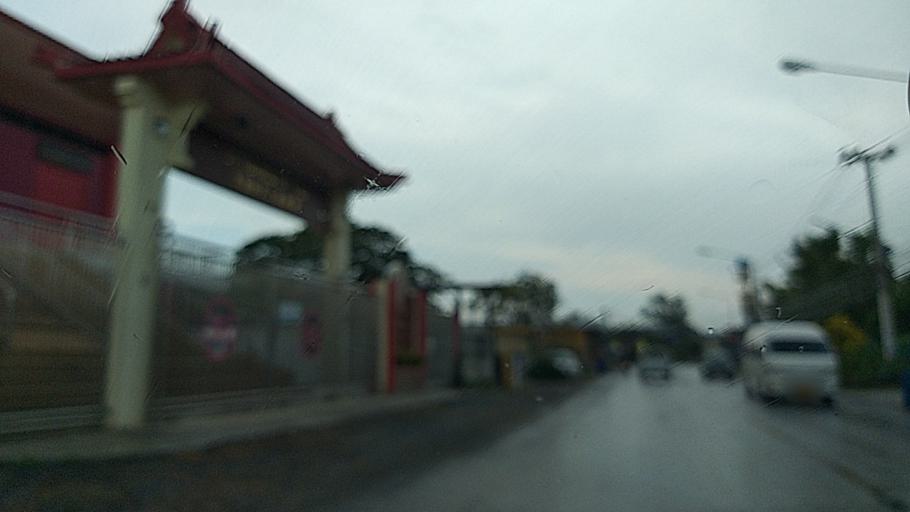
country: TH
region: Phra Nakhon Si Ayutthaya
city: Phra Nakhon Si Ayutthaya
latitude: 14.3465
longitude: 100.5417
